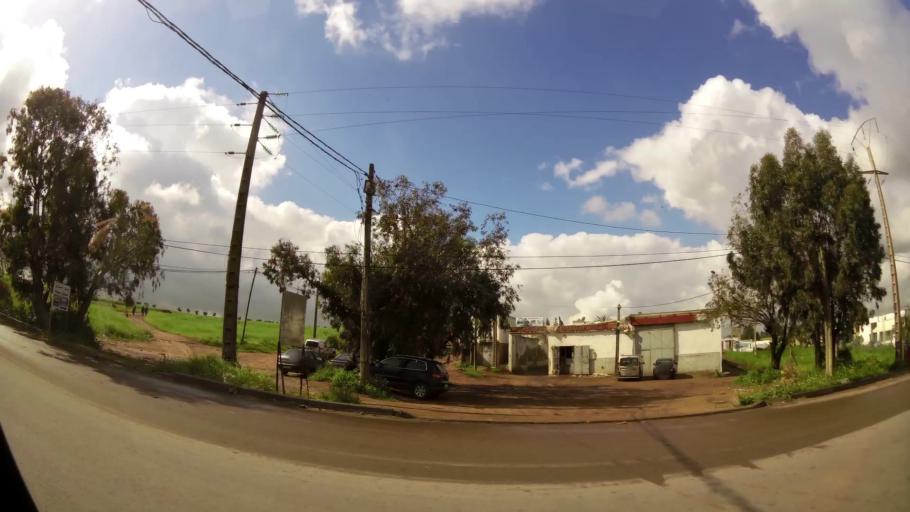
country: MA
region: Grand Casablanca
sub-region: Mediouna
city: Tit Mellil
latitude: 33.5661
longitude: -7.5035
